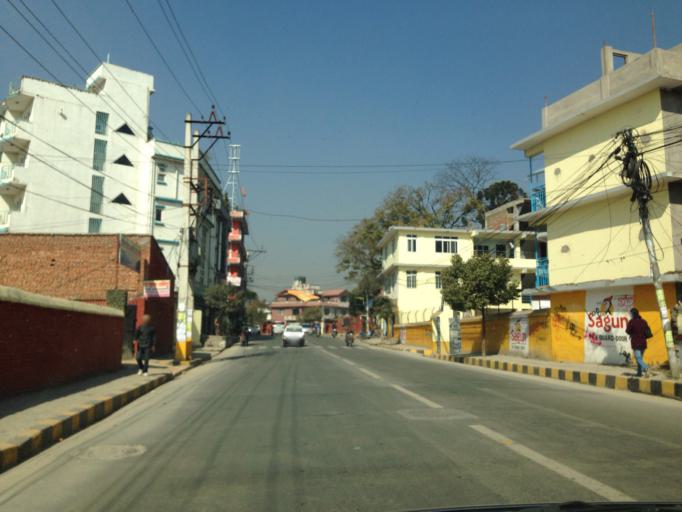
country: NP
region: Central Region
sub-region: Bagmati Zone
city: Kathmandu
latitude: 27.7302
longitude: 85.3303
